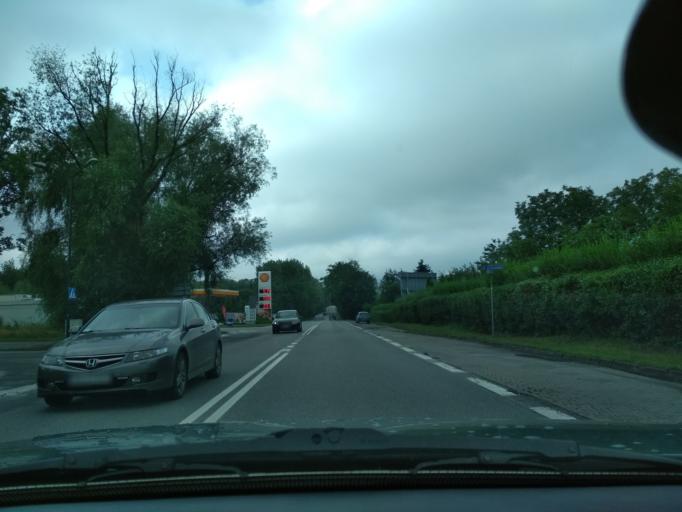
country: PL
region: Silesian Voivodeship
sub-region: Gliwice
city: Gliwice
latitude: 50.2740
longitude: 18.6613
